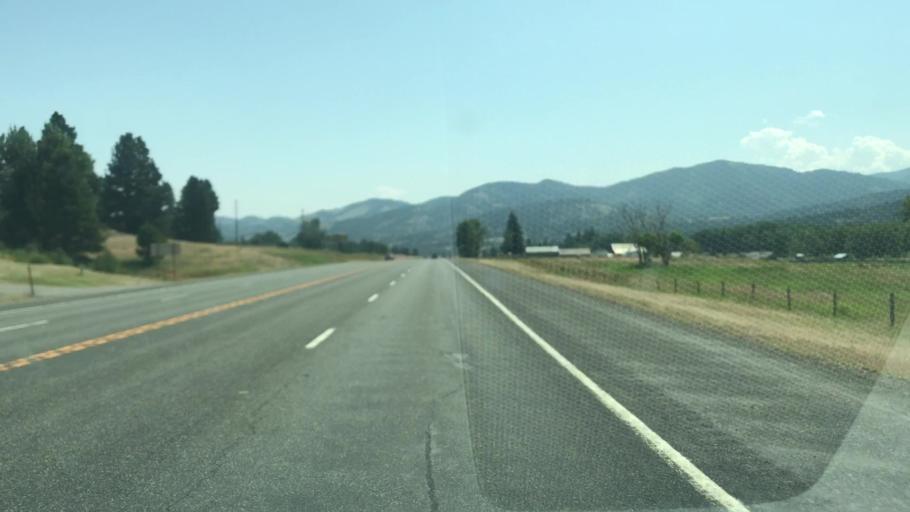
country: US
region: Montana
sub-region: Lewis and Clark County
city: Helena West Side
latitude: 46.5759
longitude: -112.1996
